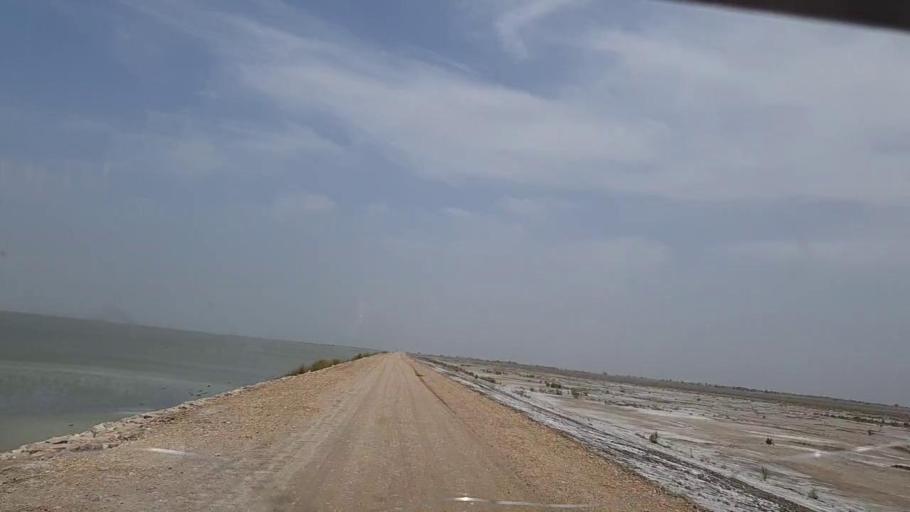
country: PK
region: Sindh
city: Sehwan
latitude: 26.4129
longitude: 67.7789
